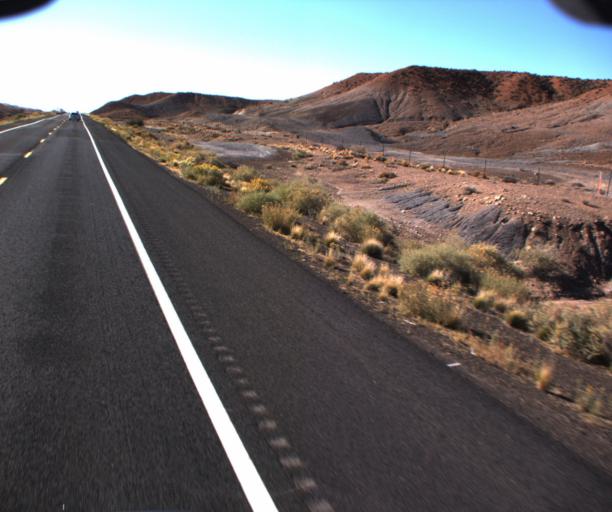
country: US
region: Arizona
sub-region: Coconino County
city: Tuba City
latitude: 36.2016
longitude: -111.3935
